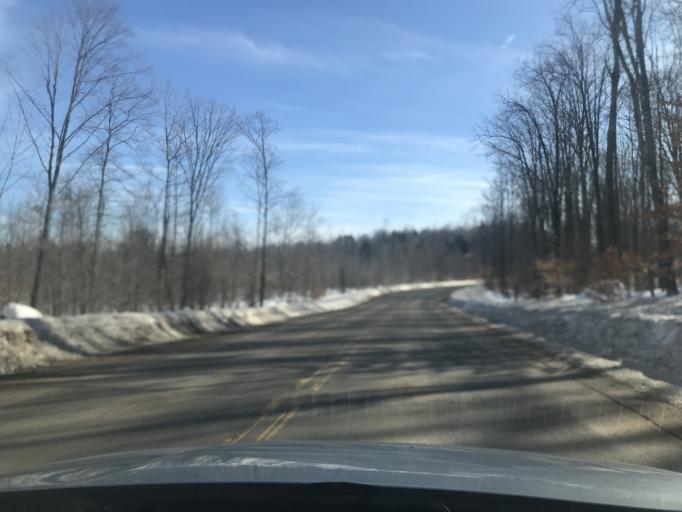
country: US
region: Michigan
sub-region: Dickinson County
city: Kingsford
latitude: 45.4078
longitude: -88.3840
